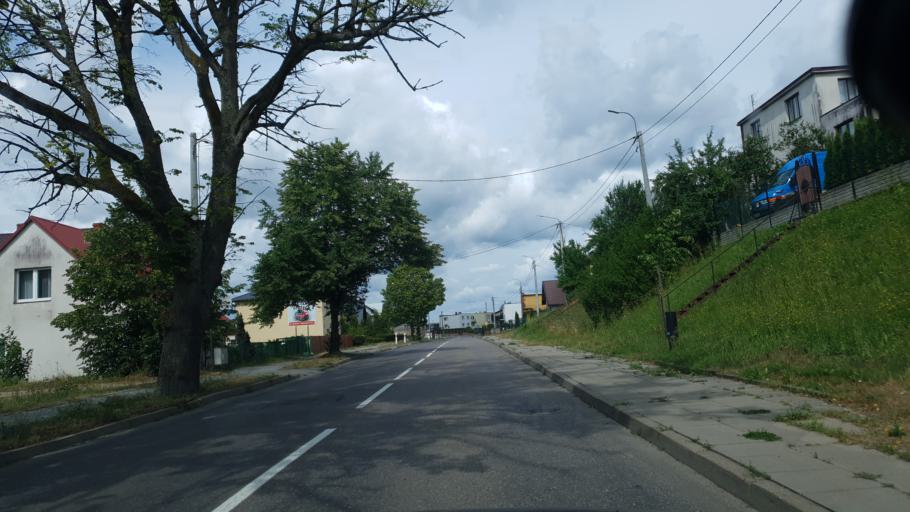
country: PL
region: Pomeranian Voivodeship
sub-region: Powiat kartuski
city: Kartuzy
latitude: 54.3216
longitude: 18.1849
